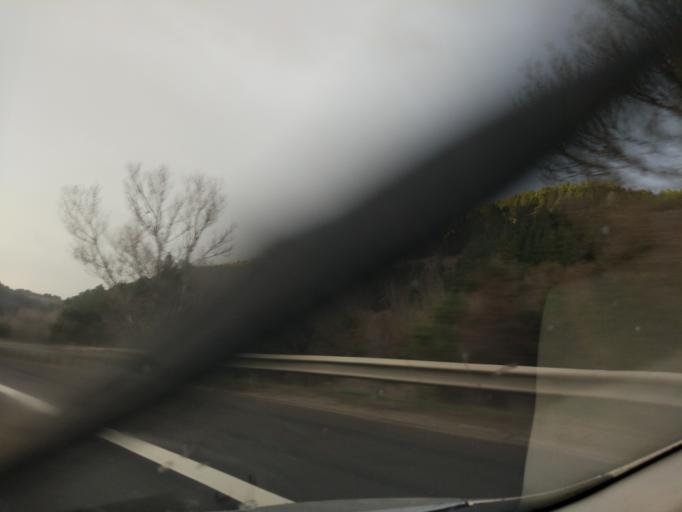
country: TR
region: Bolu
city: Bolu
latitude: 40.7397
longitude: 31.7913
